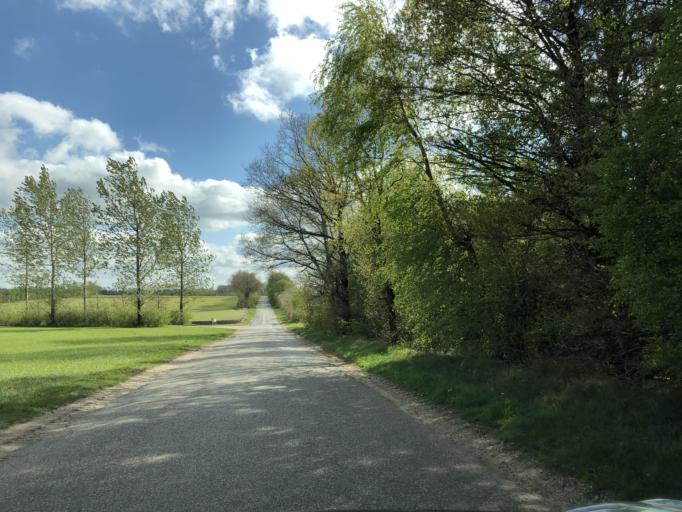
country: DK
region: Central Jutland
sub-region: Herning Kommune
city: Avlum
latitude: 56.2978
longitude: 8.7017
